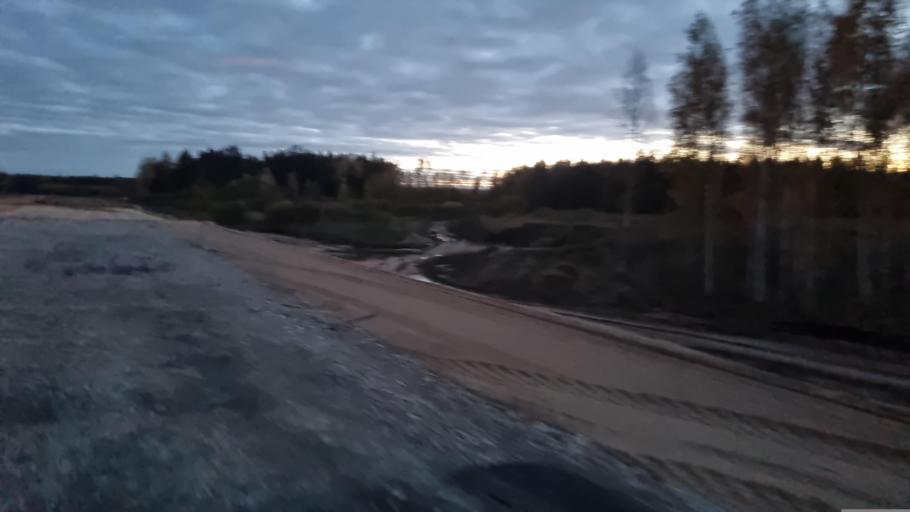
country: LV
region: Kekava
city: Balozi
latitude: 56.8402
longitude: 24.1567
